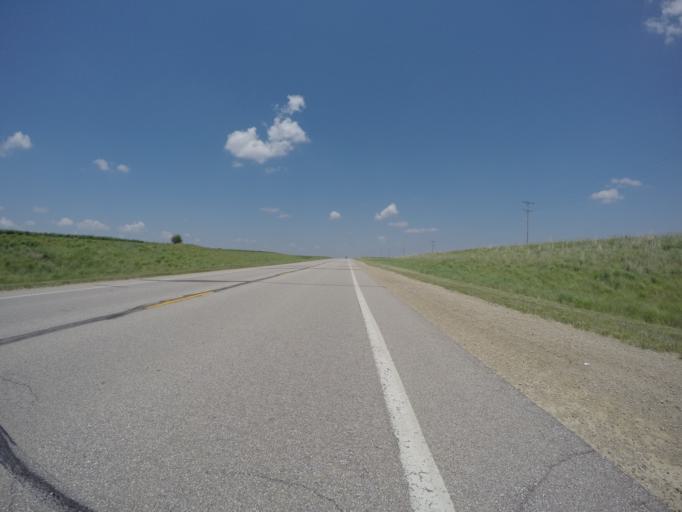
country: US
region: Kansas
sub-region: Doniphan County
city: Troy
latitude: 39.7468
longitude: -95.1438
